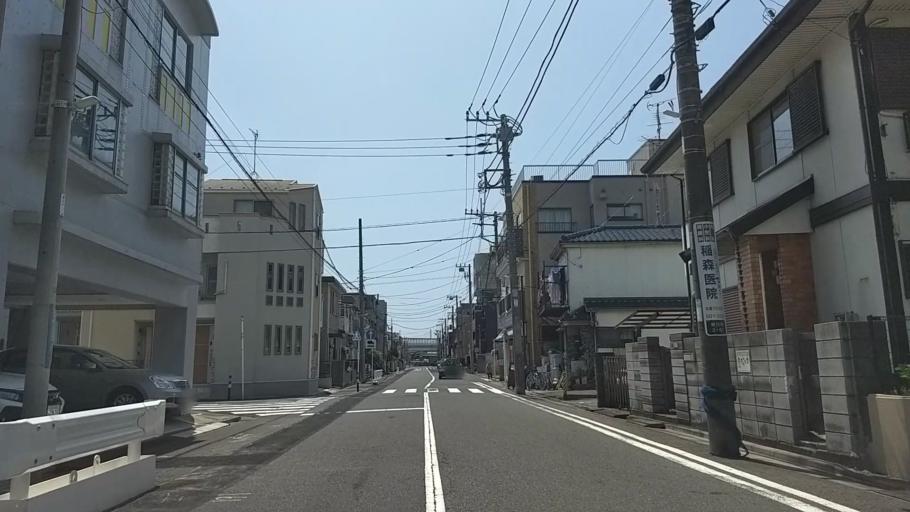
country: JP
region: Kanagawa
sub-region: Kawasaki-shi
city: Kawasaki
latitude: 35.5053
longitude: 139.6986
